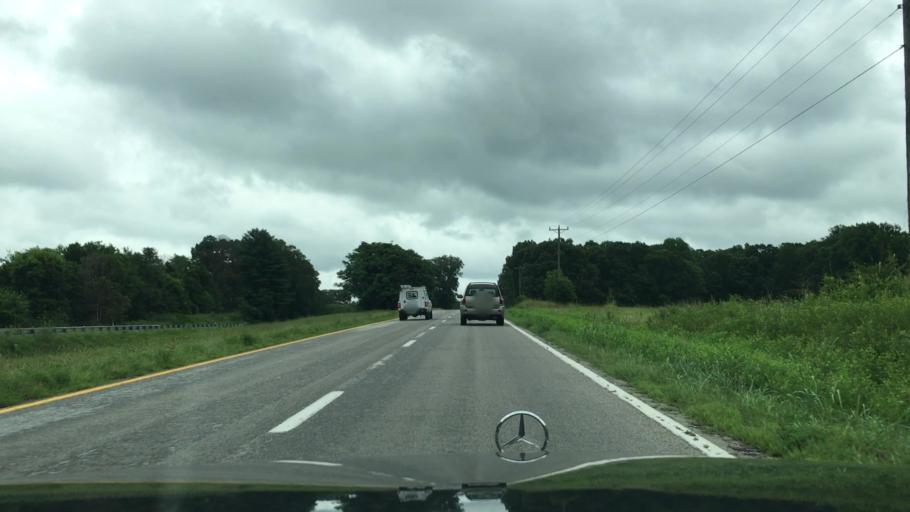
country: US
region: Virginia
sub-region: Prince Edward County
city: Hampden Sydney
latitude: 37.3068
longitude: -78.5154
